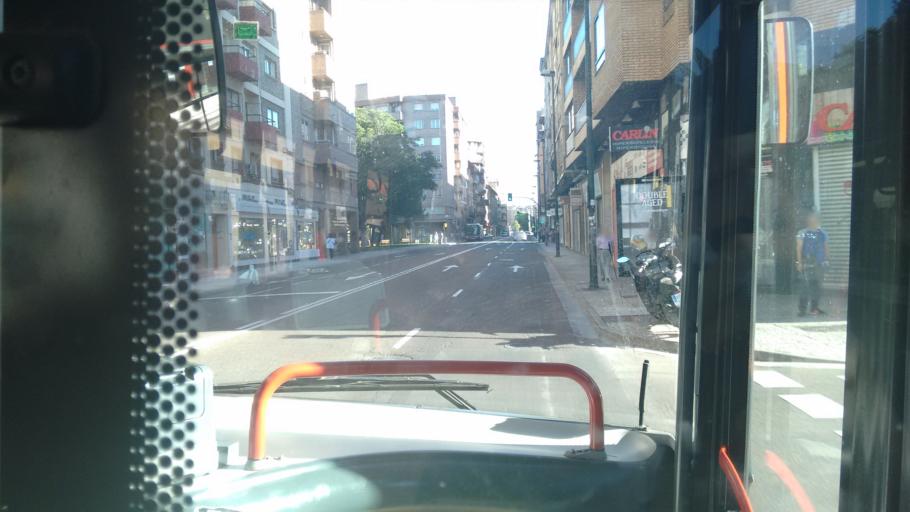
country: ES
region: Aragon
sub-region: Provincia de Zaragoza
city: Zaragoza
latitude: 41.6451
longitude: -0.8728
